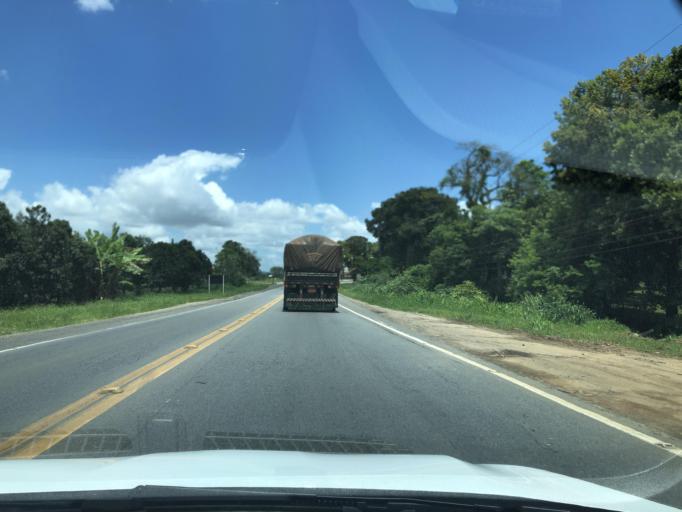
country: BR
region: Santa Catarina
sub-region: Sao Francisco Do Sul
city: Sao Francisco do Sul
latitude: -26.3702
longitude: -48.6890
